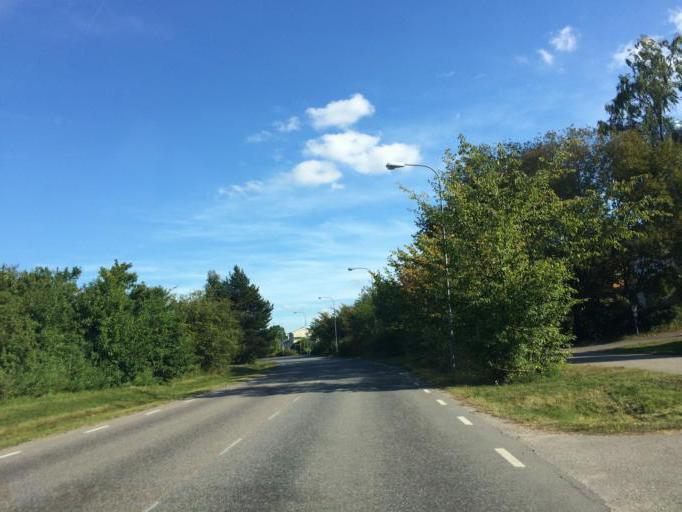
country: SE
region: Stockholm
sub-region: Upplands Vasby Kommun
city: Upplands Vaesby
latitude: 59.4954
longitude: 17.9376
